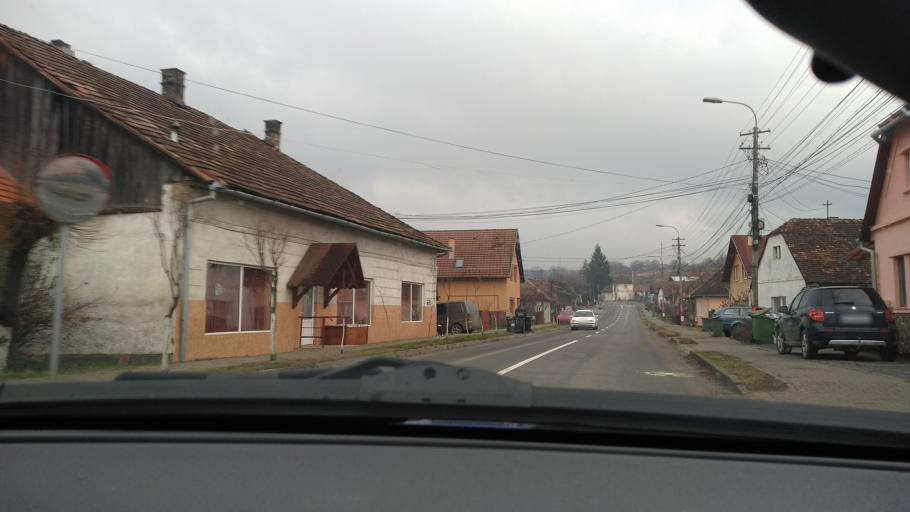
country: RO
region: Mures
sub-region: Oras Sovata
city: Sovata
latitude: 46.5825
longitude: 25.0579
